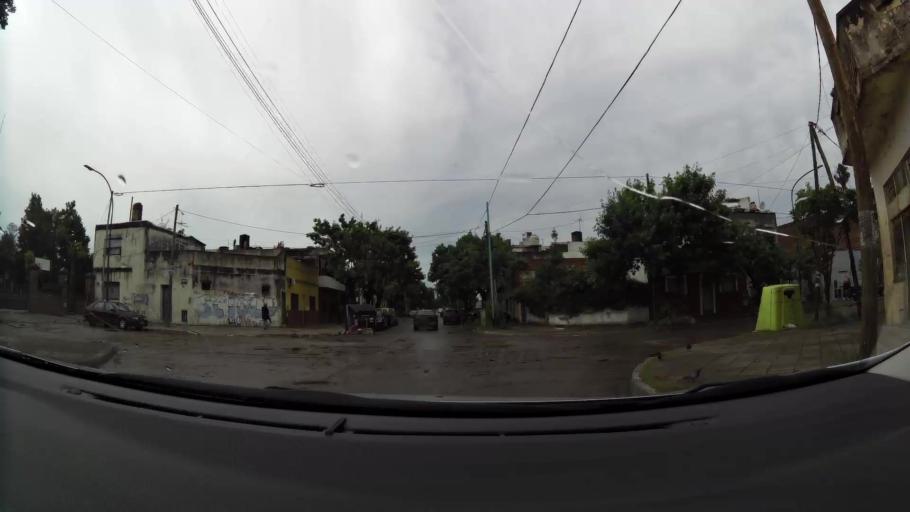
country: AR
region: Buenos Aires F.D.
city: Villa Lugano
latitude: -34.6595
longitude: -58.4466
